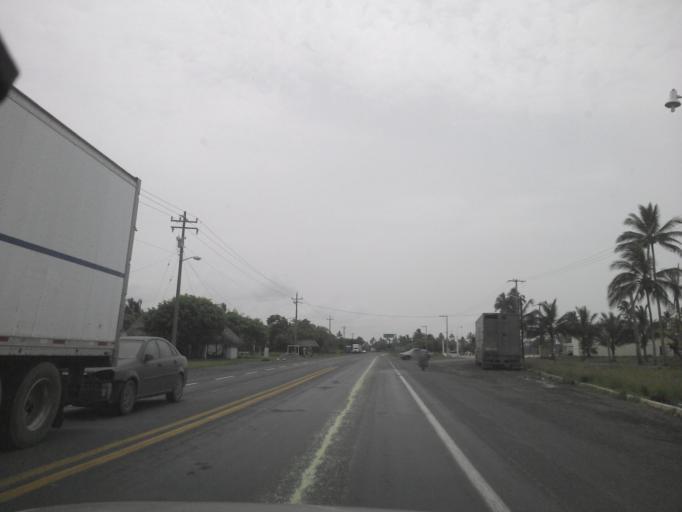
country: MX
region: Veracruz
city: Tecolutla
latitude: 20.3783
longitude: -96.9272
